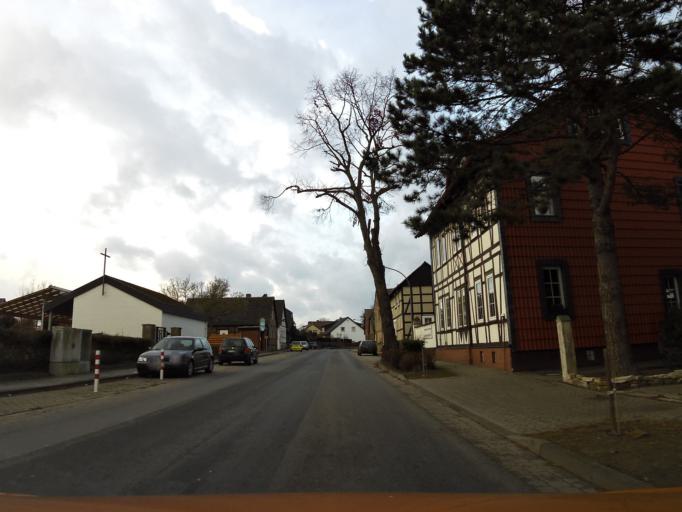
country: DE
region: Lower Saxony
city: Gross Twulpstedt
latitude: 52.3799
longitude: 10.9019
